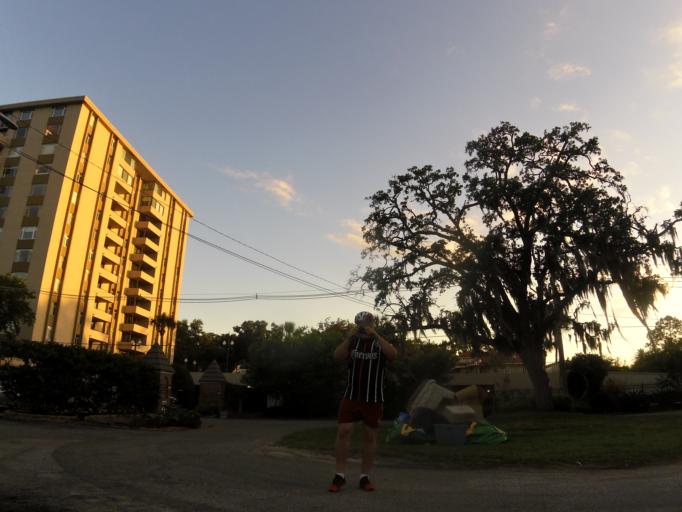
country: US
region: Florida
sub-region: Duval County
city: Jacksonville
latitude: 30.3029
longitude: -81.6950
